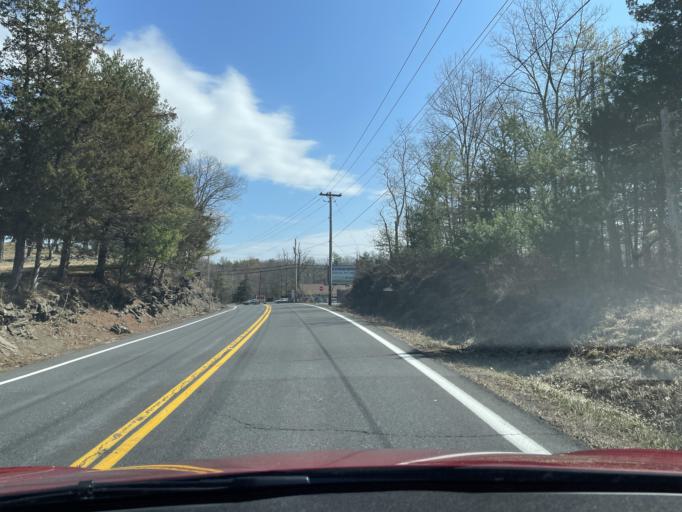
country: US
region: New York
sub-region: Ulster County
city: Manorville
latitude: 42.0728
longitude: -74.0317
